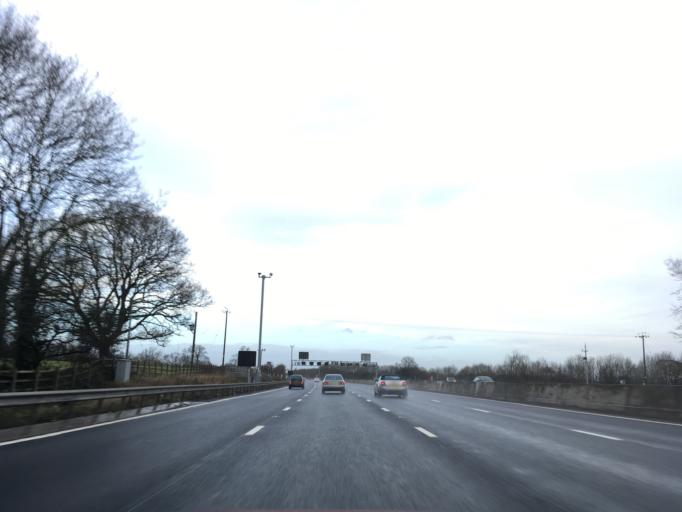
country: GB
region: England
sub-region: Worcestershire
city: Droitwich
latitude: 52.2470
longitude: -2.1335
